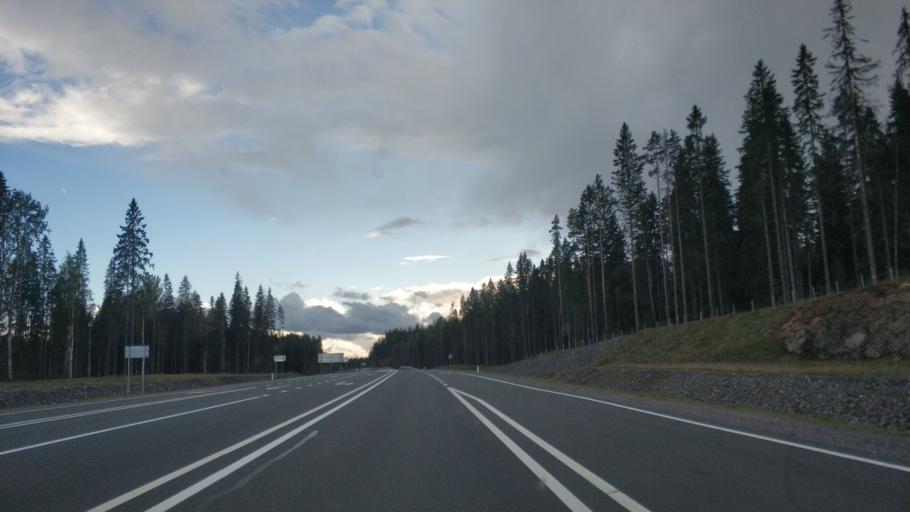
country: RU
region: Republic of Karelia
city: Lakhdenpokh'ya
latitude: 61.4647
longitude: 30.0003
